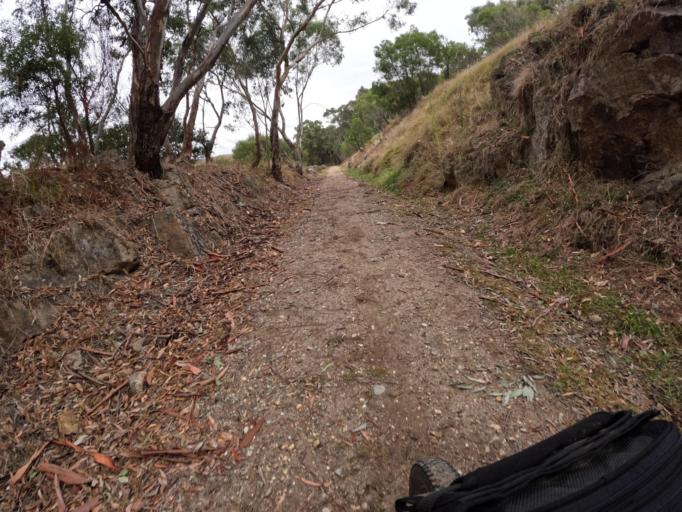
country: AU
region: New South Wales
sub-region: Greater Hume Shire
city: Holbrook
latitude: -36.1775
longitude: 147.3820
